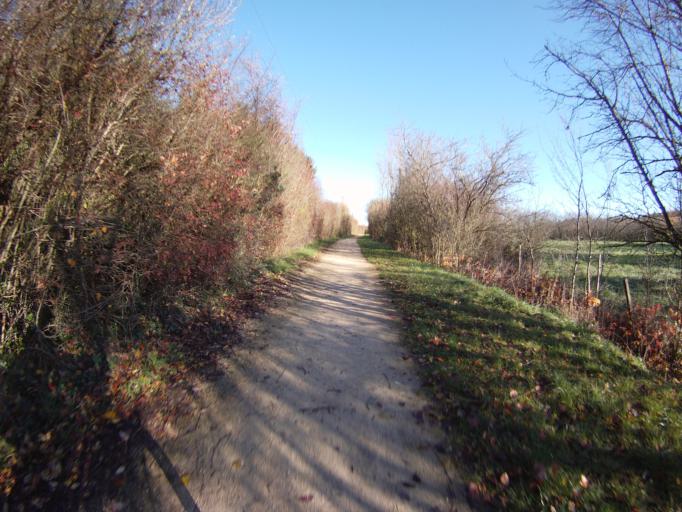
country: FR
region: Lorraine
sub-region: Departement de Meurthe-et-Moselle
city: Bouxieres-aux-Chenes
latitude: 48.7949
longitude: 6.2349
